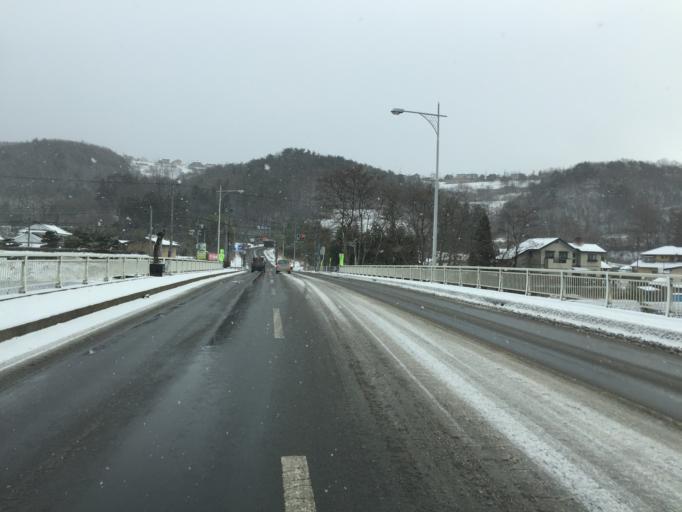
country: JP
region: Fukushima
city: Fukushima-shi
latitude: 37.7266
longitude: 140.4724
